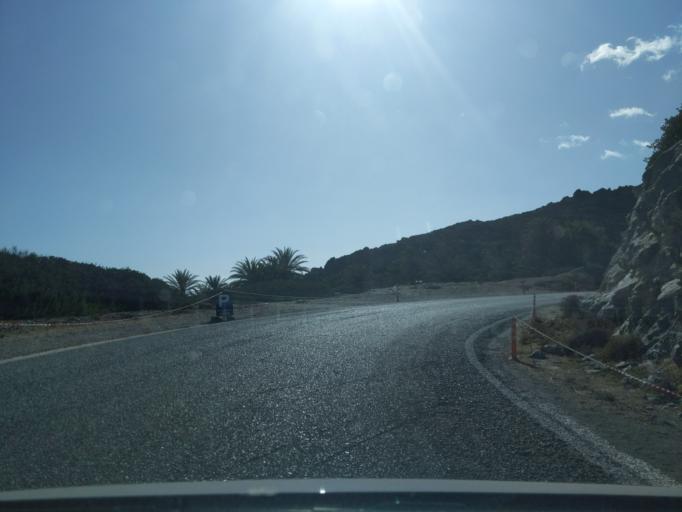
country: GR
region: Crete
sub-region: Nomos Lasithiou
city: Palekastro
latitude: 35.2542
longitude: 26.2640
